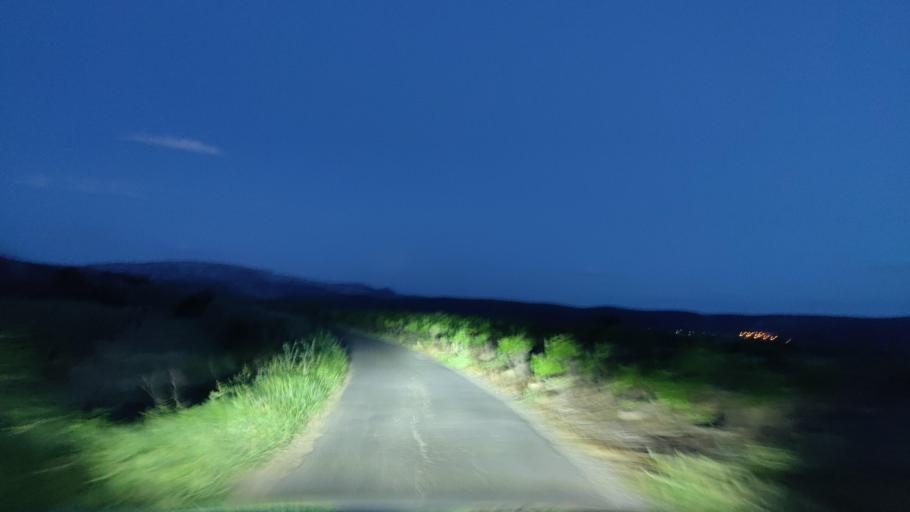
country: FR
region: Languedoc-Roussillon
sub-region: Departement des Pyrenees-Orientales
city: Estagel
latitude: 42.8824
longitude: 2.7246
